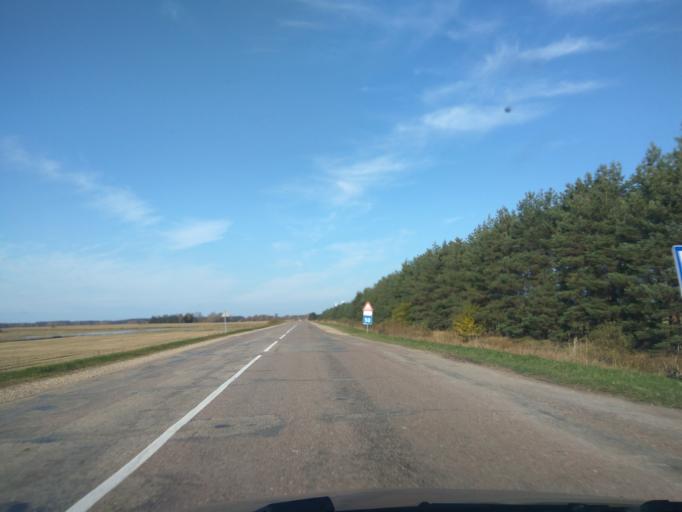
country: LV
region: Ventspils Rajons
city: Piltene
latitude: 57.2548
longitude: 21.5904
